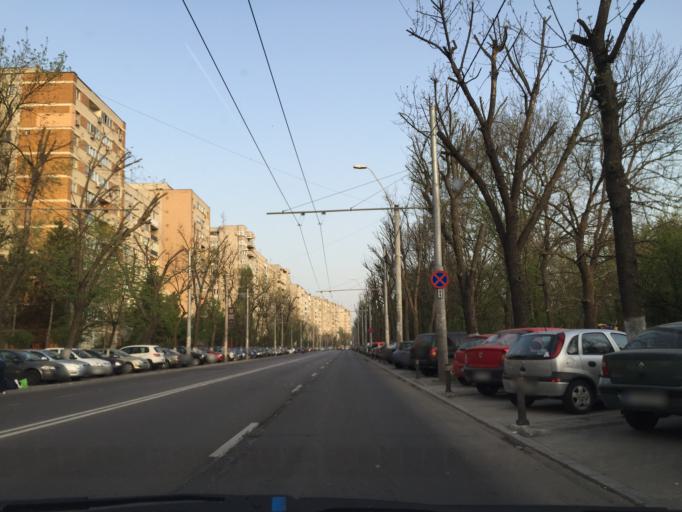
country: RO
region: Bucuresti
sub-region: Municipiul Bucuresti
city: Bucuresti
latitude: 44.4117
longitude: 26.1073
